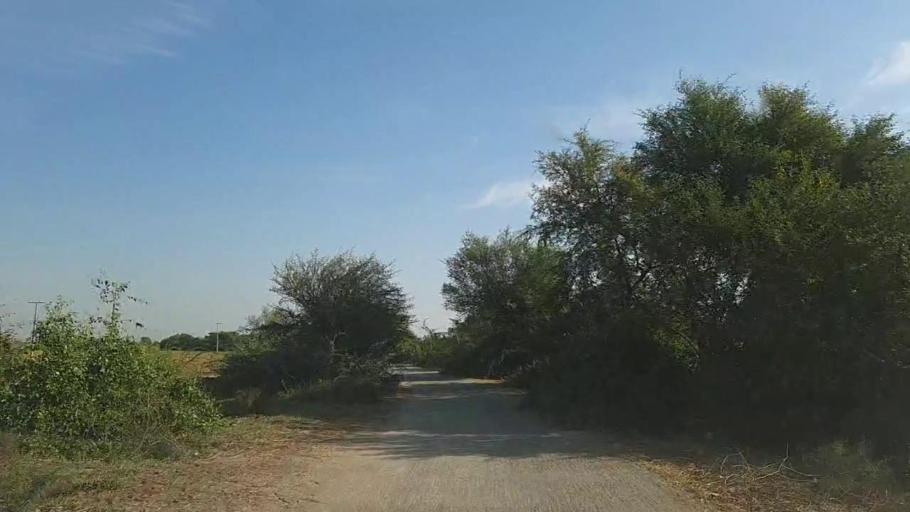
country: PK
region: Sindh
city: Bulri
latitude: 24.7959
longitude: 68.3397
